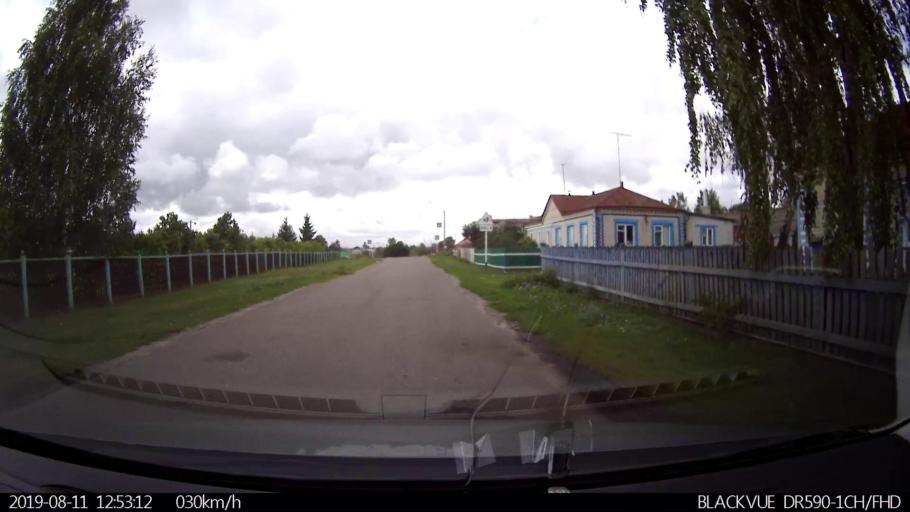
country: RU
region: Ulyanovsk
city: Ignatovka
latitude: 53.8756
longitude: 47.6524
